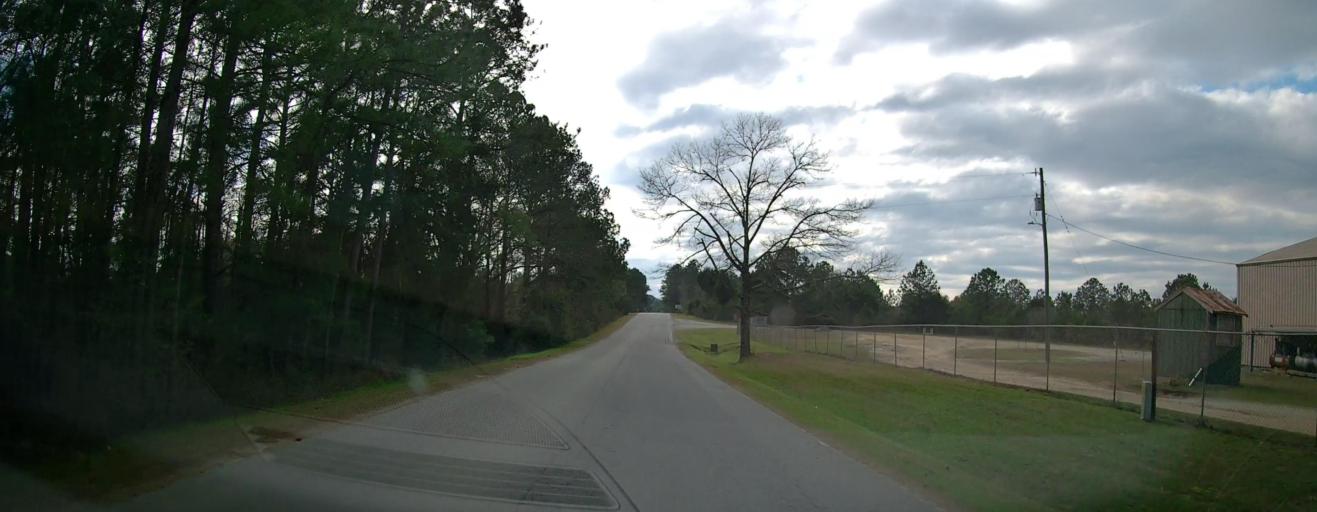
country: US
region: Georgia
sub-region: Taylor County
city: Butler
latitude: 32.4622
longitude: -84.3709
